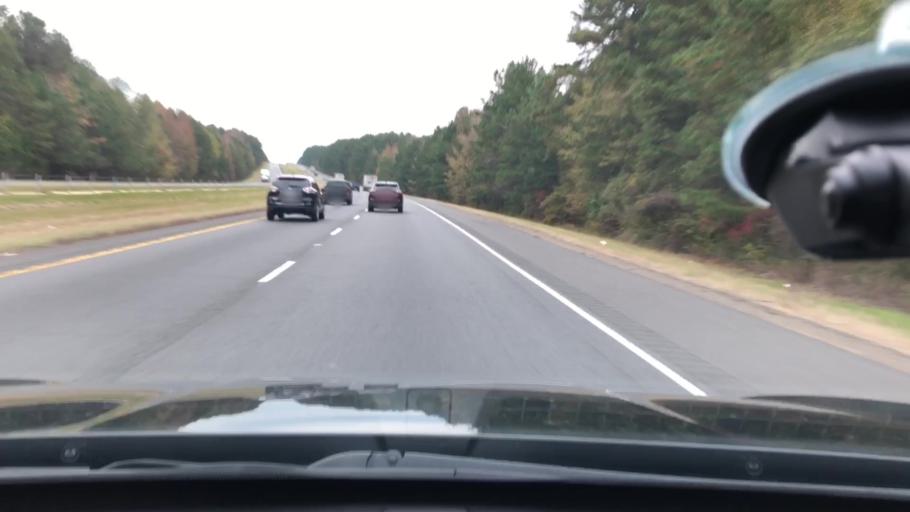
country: US
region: Arkansas
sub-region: Clark County
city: Gurdon
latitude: 34.0354
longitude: -93.1438
